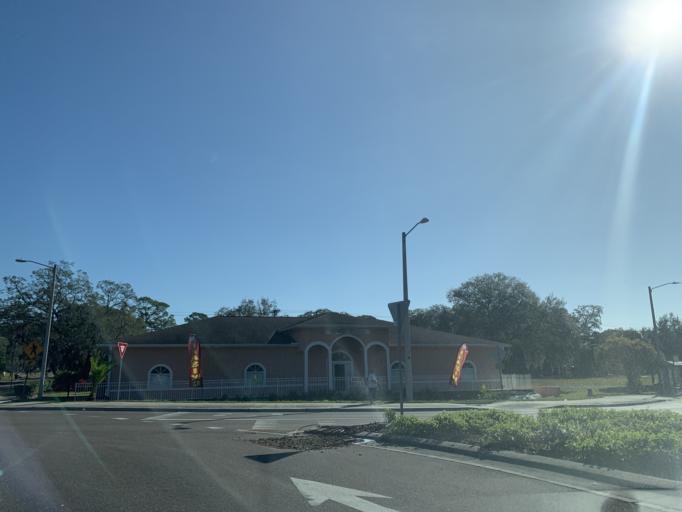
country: US
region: Florida
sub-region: Hillsborough County
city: Temple Terrace
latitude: 28.0214
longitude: -82.4151
